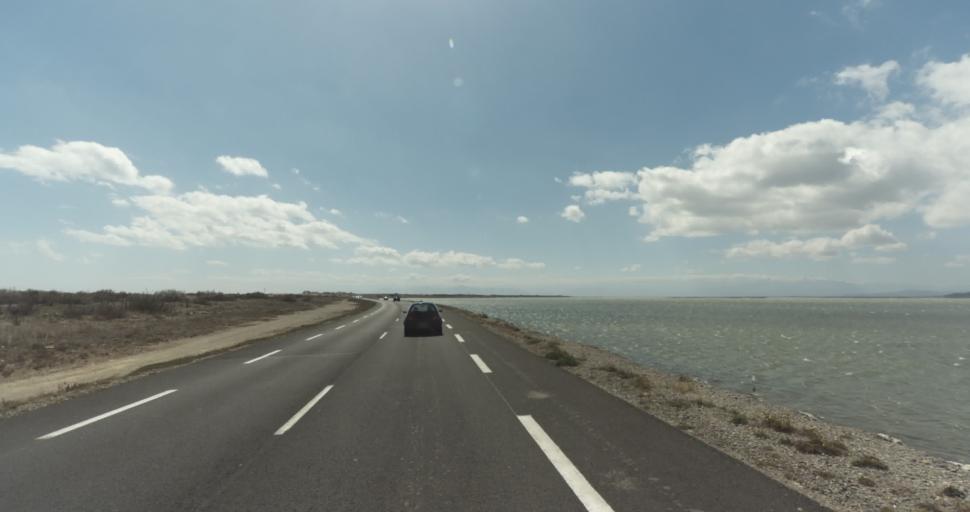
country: FR
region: Languedoc-Roussillon
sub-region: Departement de l'Aude
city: Leucate
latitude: 42.8949
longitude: 3.0482
